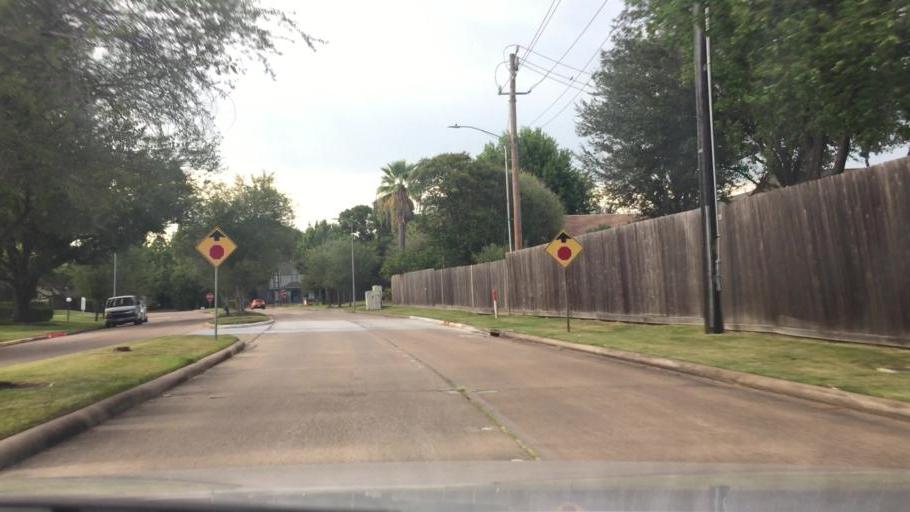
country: US
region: Texas
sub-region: Harris County
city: Bunker Hill Village
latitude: 29.7402
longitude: -95.5813
